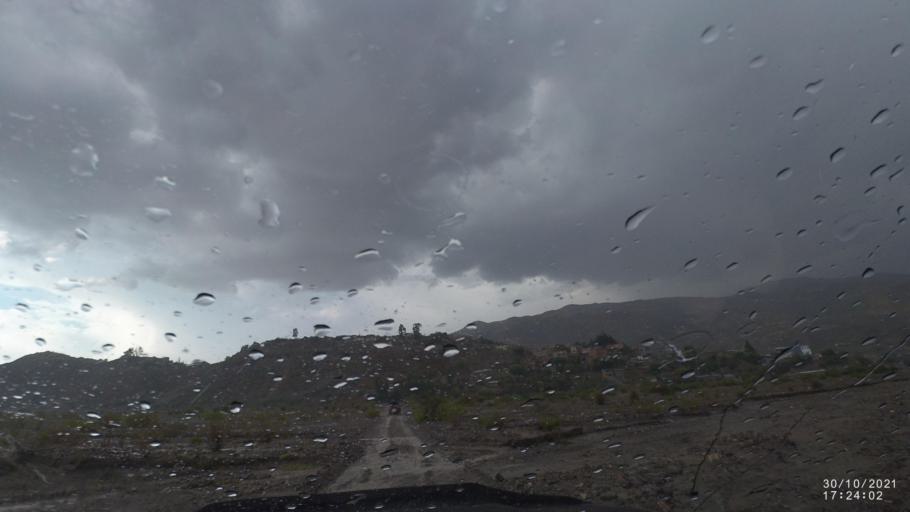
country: BO
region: Cochabamba
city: Colchani
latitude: -17.5200
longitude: -66.6223
